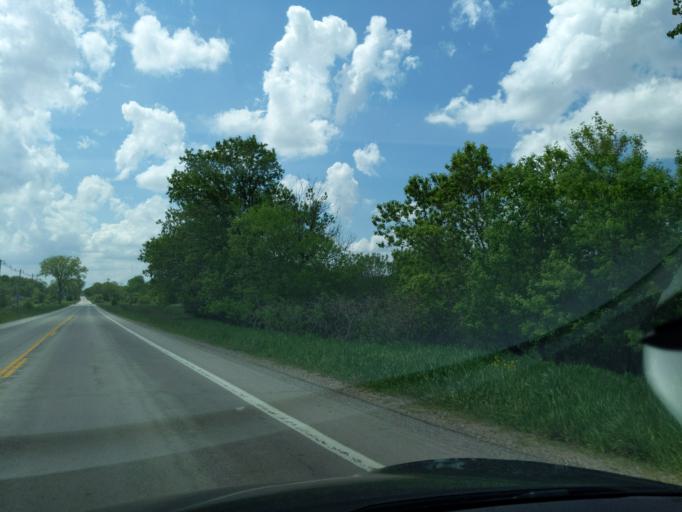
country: US
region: Michigan
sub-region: Ingham County
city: Mason
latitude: 42.5559
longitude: -84.3359
